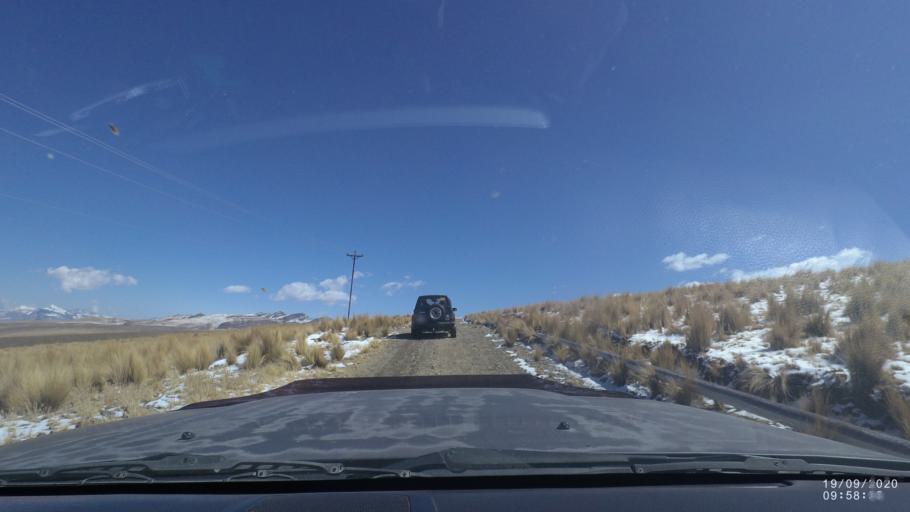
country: BO
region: Cochabamba
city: Cochabamba
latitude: -17.3087
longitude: -66.0875
